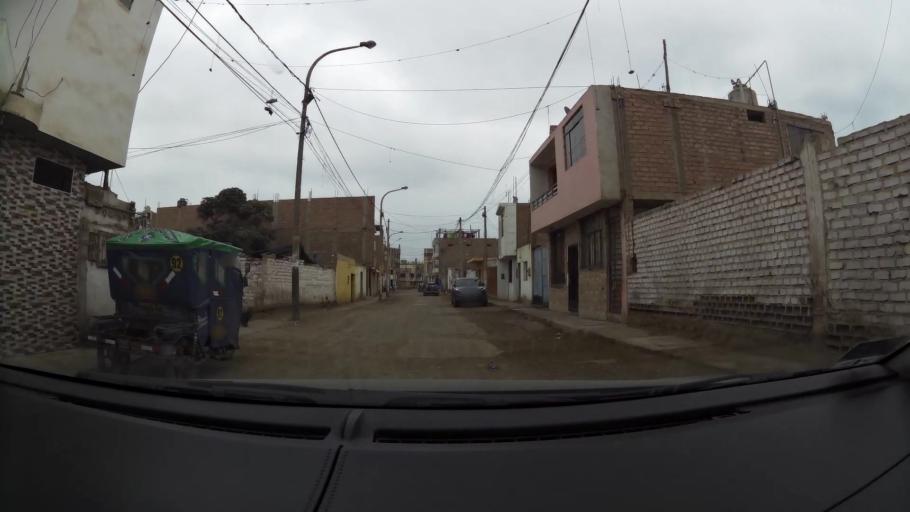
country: PE
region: Lima
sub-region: Provincia de Huaral
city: Huaral
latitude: -11.4992
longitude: -77.2025
